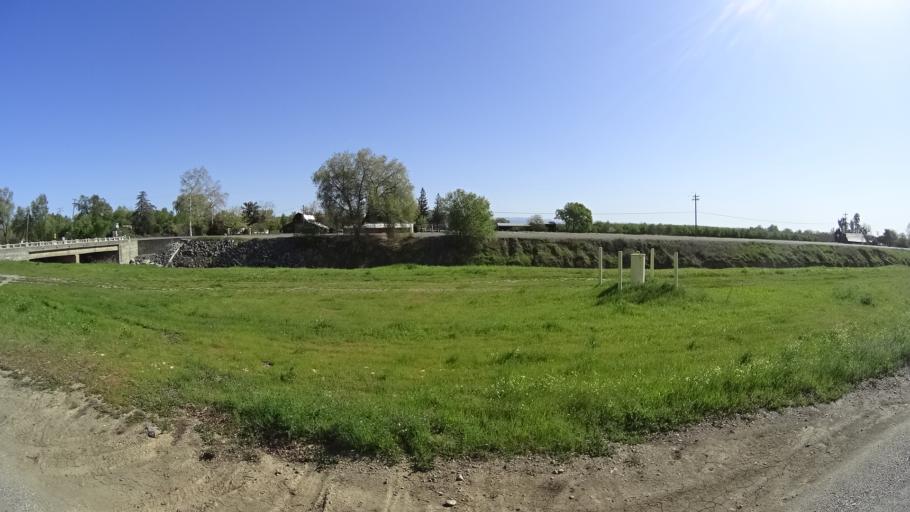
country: US
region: California
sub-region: Glenn County
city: Hamilton City
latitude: 39.7836
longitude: -122.0464
